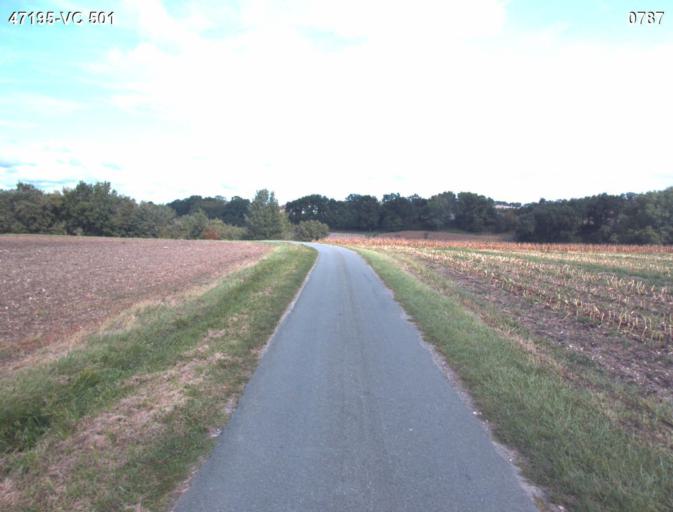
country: FR
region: Aquitaine
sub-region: Departement du Lot-et-Garonne
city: Nerac
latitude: 44.1017
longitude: 0.3178
